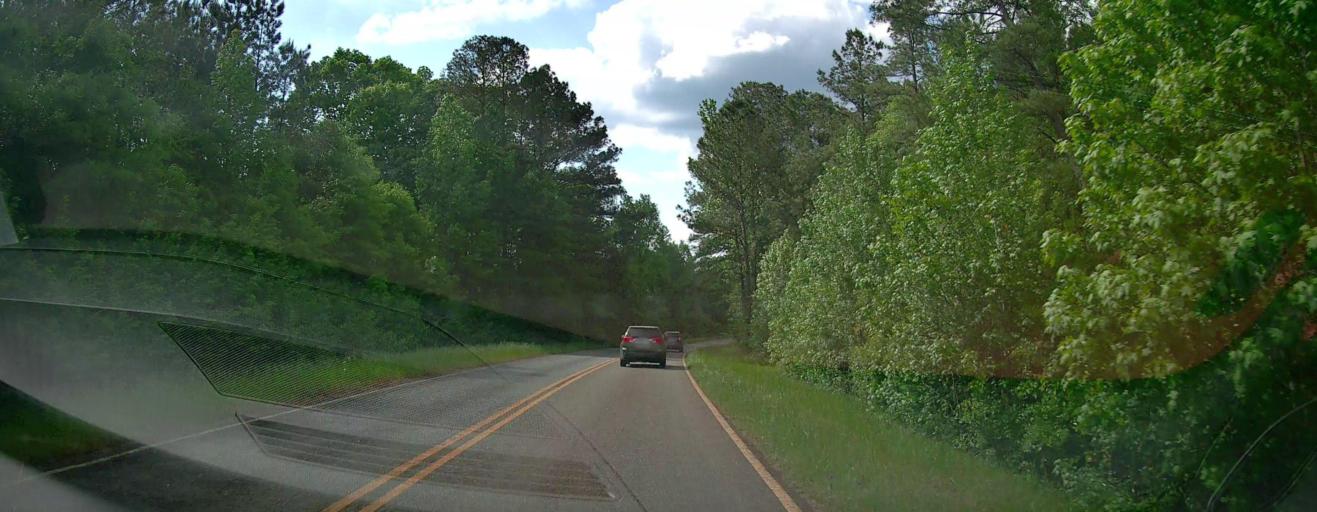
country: US
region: Georgia
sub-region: Laurens County
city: East Dublin
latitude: 32.7395
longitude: -82.9189
